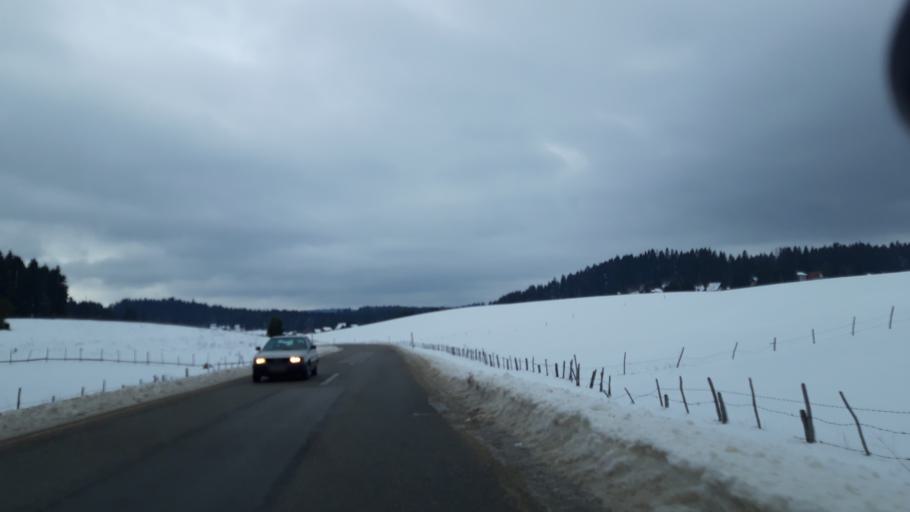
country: BA
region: Republika Srpska
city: Han Pijesak
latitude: 44.0983
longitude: 18.9634
